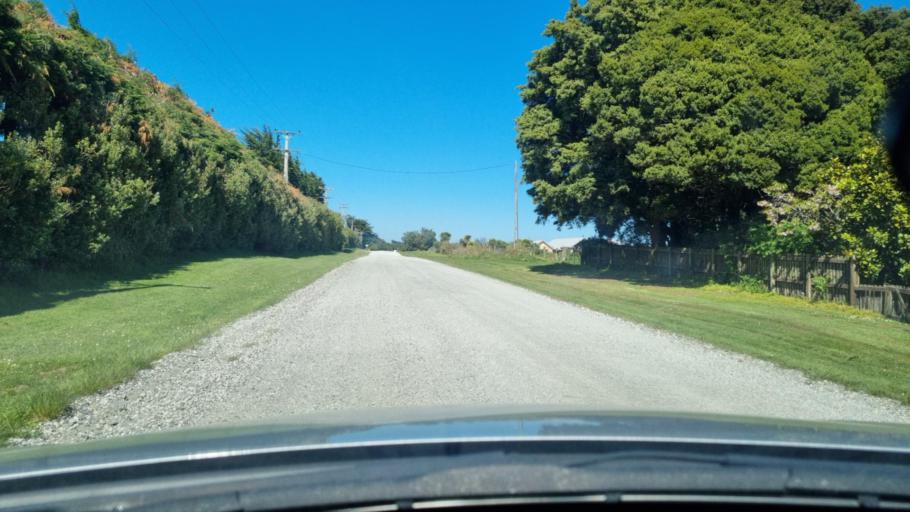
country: NZ
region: Southland
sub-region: Invercargill City
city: Invercargill
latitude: -46.4419
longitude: 168.2784
